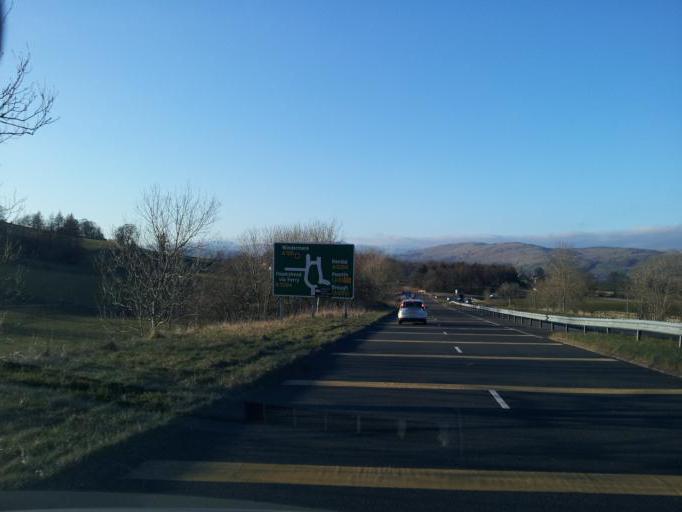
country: GB
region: England
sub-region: Cumbria
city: Kendal
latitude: 54.3409
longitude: -2.7733
